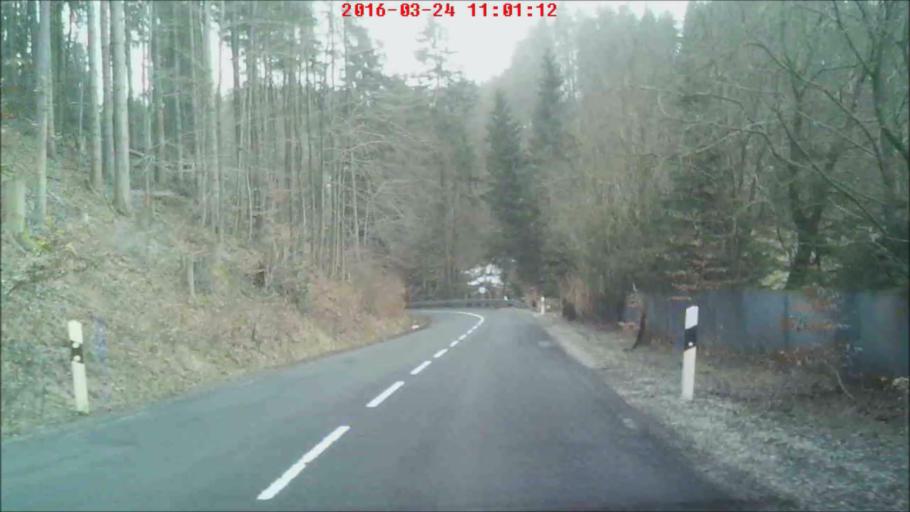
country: DE
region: Thuringia
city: Neustadt am Rennsteig
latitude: 50.5576
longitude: 10.9281
